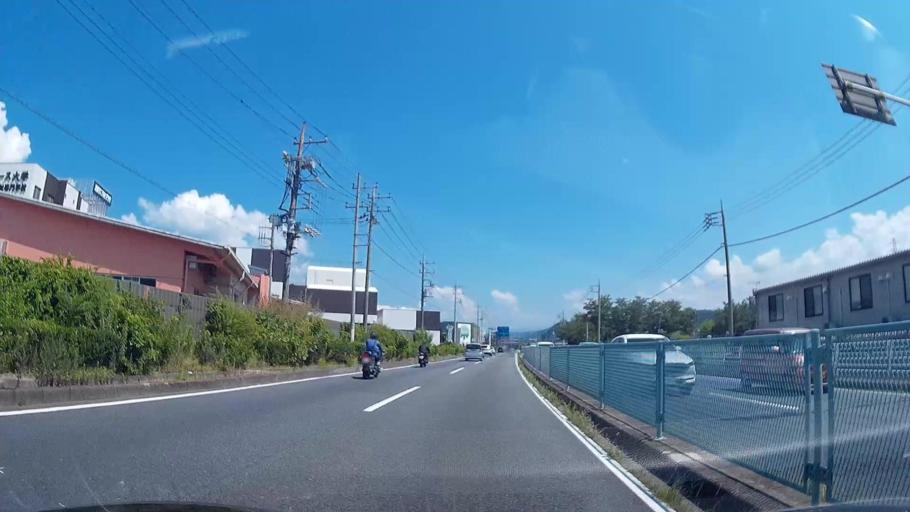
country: JP
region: Gunma
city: Shibukawa
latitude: 36.4923
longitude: 139.0118
